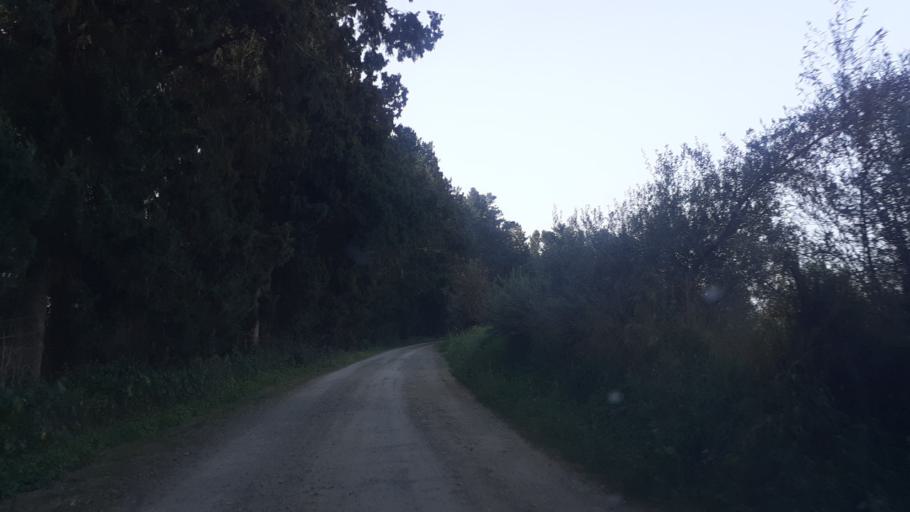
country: CY
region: Limassol
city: Ypsonas
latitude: 34.6587
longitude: 32.9792
